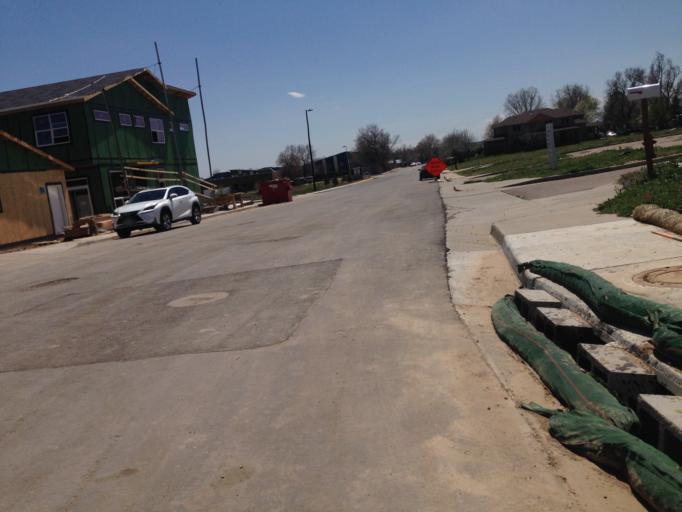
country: US
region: Colorado
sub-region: Boulder County
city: Louisville
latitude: 39.9890
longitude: -105.1175
